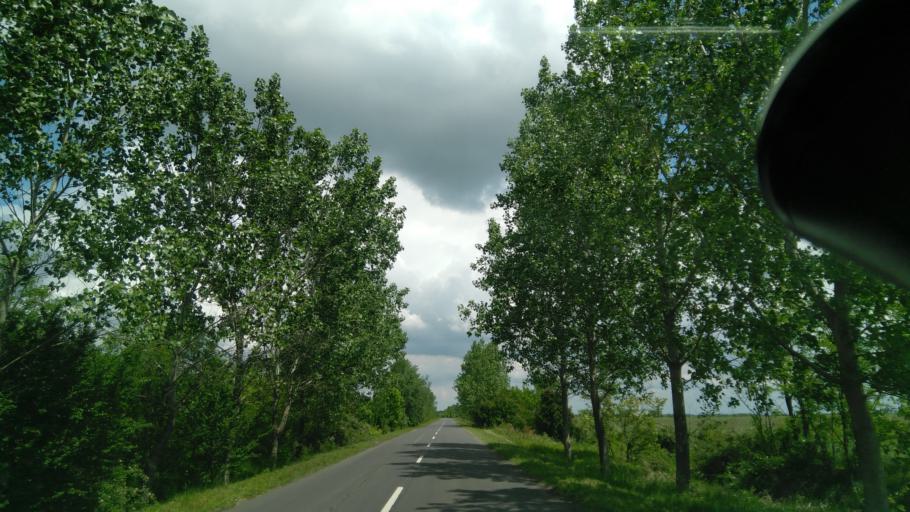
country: HU
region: Bekes
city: Gyomaendrod
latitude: 46.9767
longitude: 20.8825
